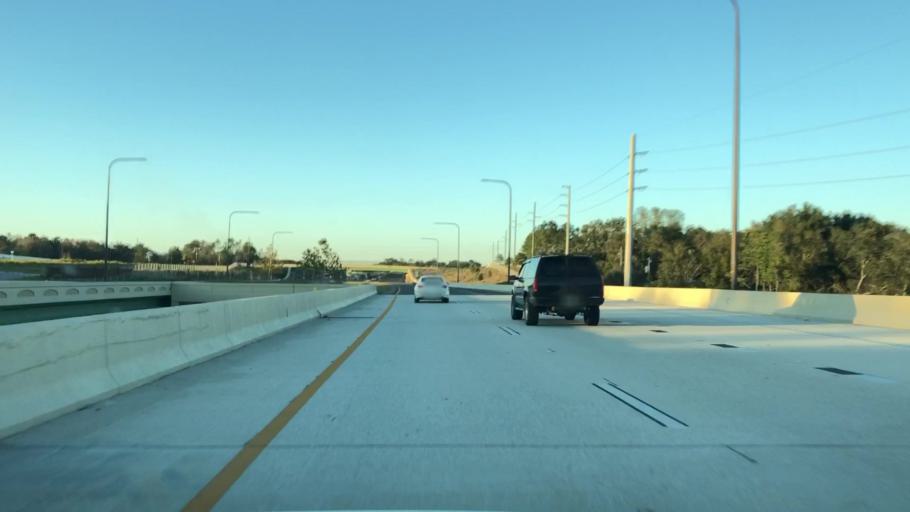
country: US
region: Florida
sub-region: Orange County
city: Zellwood
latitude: 28.7046
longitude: -81.5593
